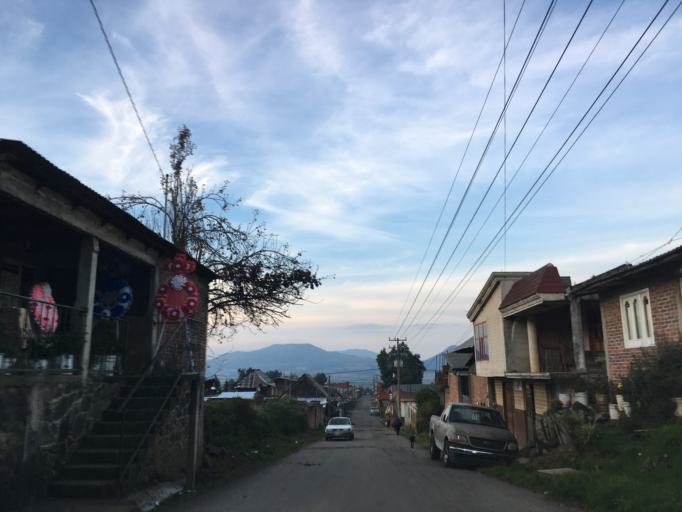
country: MX
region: Michoacan
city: Charapan
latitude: 19.6076
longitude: -102.2335
